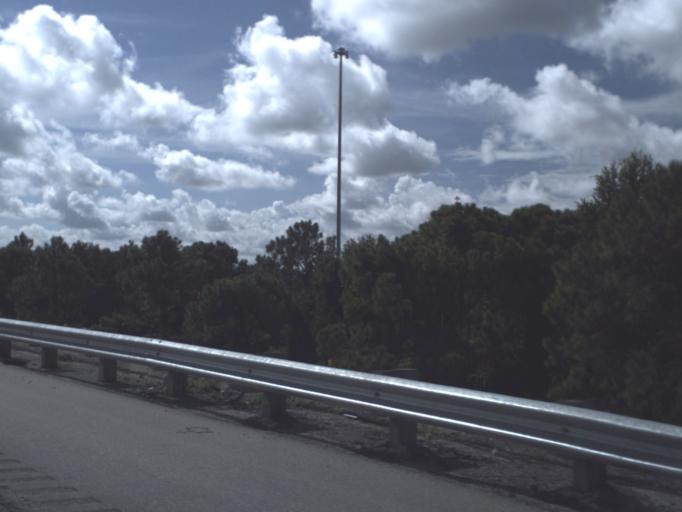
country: US
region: Florida
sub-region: Sarasota County
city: Venice Gardens
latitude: 27.1116
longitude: -82.3855
